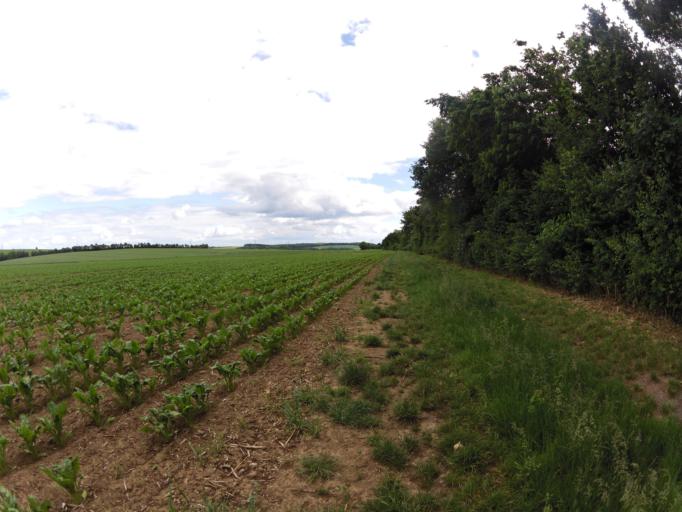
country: DE
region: Bavaria
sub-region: Regierungsbezirk Unterfranken
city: Gaukonigshofen
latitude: 49.6629
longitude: 10.0144
